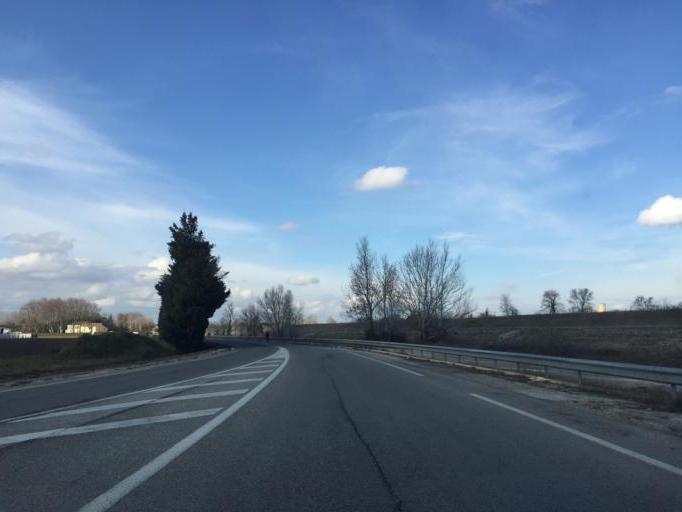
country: FR
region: Languedoc-Roussillon
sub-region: Departement du Gard
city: Roquemaure
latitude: 44.0451
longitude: 4.7939
